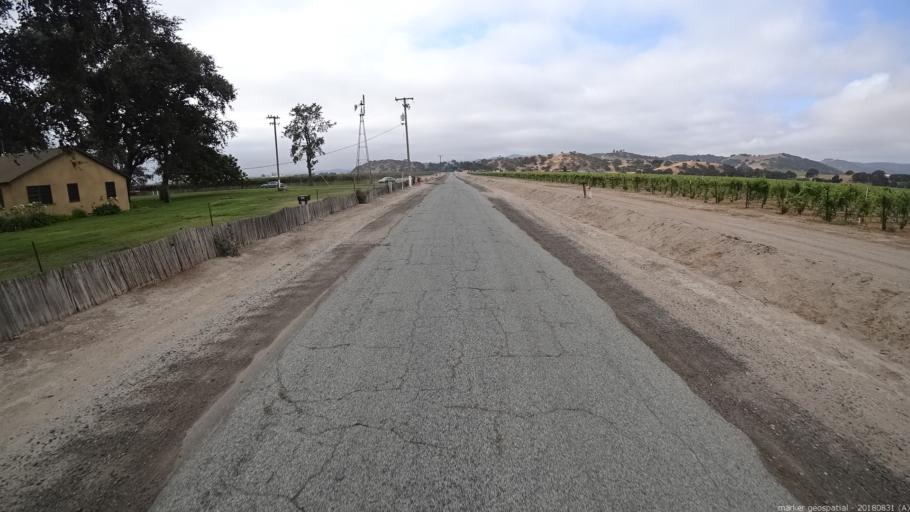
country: US
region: California
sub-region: Monterey County
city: King City
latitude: 36.1474
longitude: -121.1006
